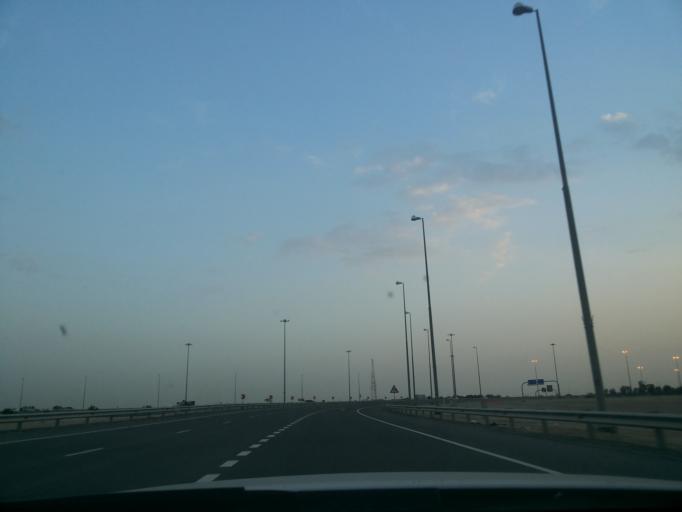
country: AE
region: Abu Dhabi
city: Abu Dhabi
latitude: 24.6935
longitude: 54.7764
